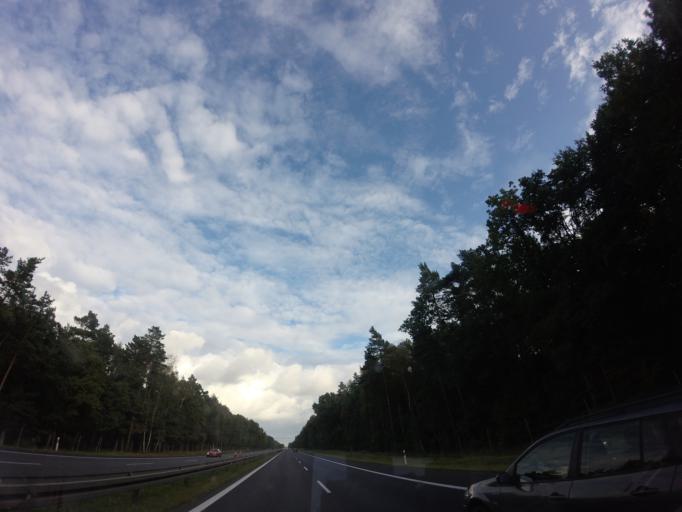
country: PL
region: West Pomeranian Voivodeship
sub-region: Powiat gryfinski
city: Stare Czarnowo
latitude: 53.3601
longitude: 14.7664
